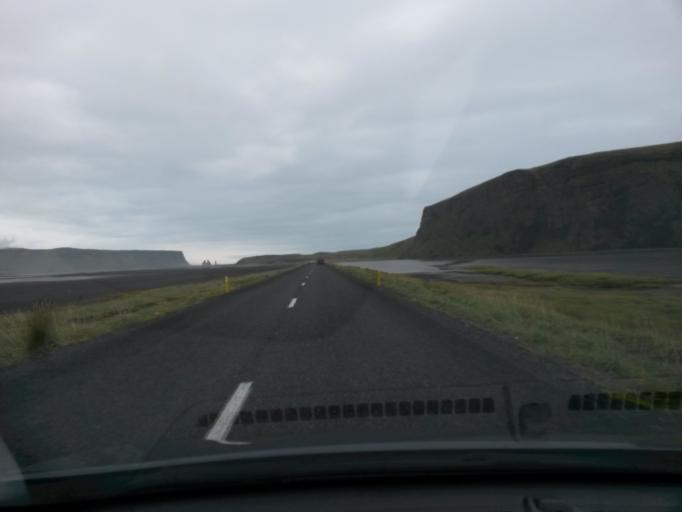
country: IS
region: South
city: Vestmannaeyjar
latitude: 63.4133
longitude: -19.1380
